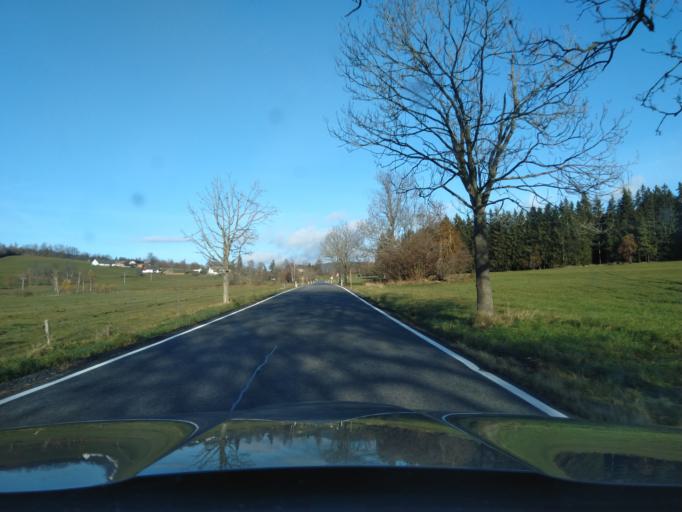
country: CZ
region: Jihocesky
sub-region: Okres Prachatice
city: Stachy
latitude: 49.1058
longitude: 13.6564
